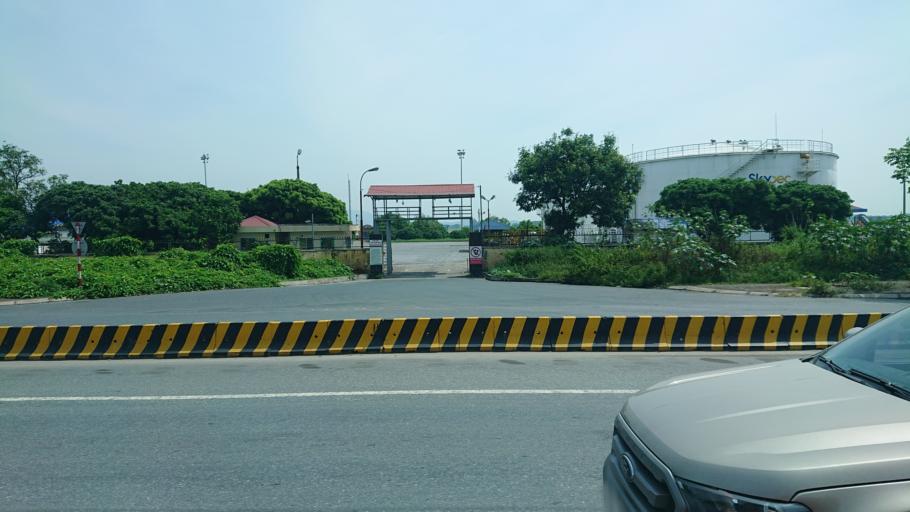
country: VN
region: Ha Noi
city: Soc Son
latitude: 21.2096
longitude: 105.8148
